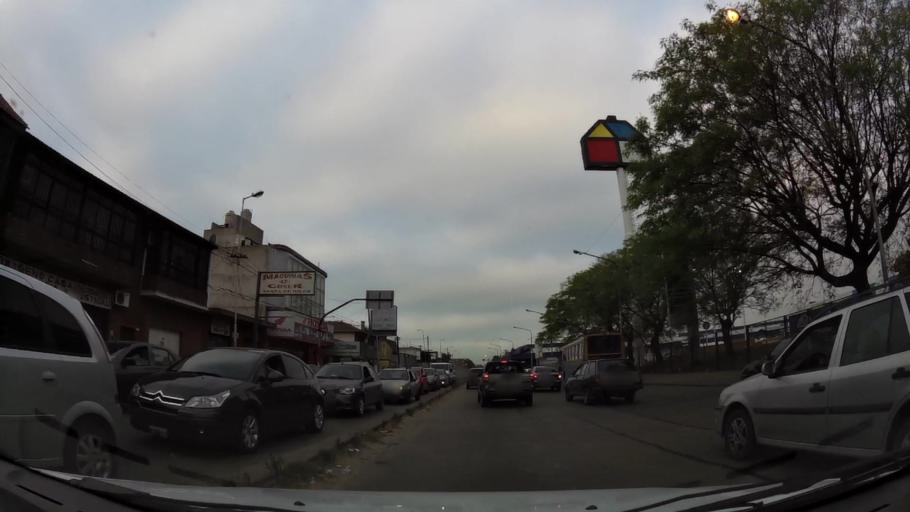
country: AR
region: Buenos Aires
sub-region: Partido de Moron
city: Moron
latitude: -34.6652
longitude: -58.5995
